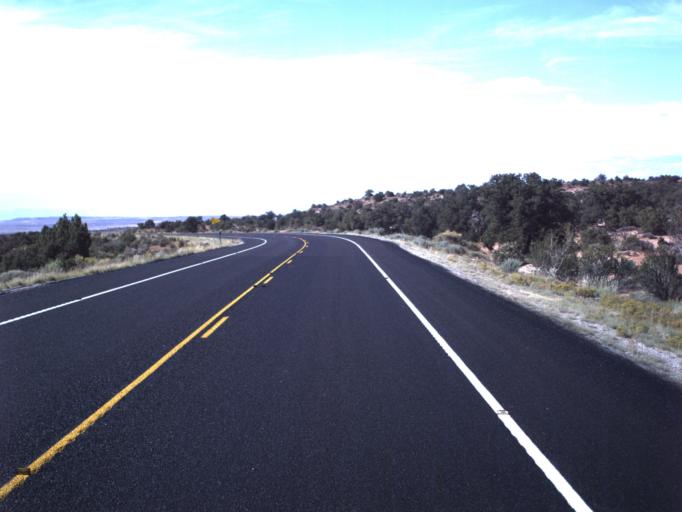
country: US
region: Utah
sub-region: Grand County
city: Moab
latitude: 38.5754
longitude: -109.7941
